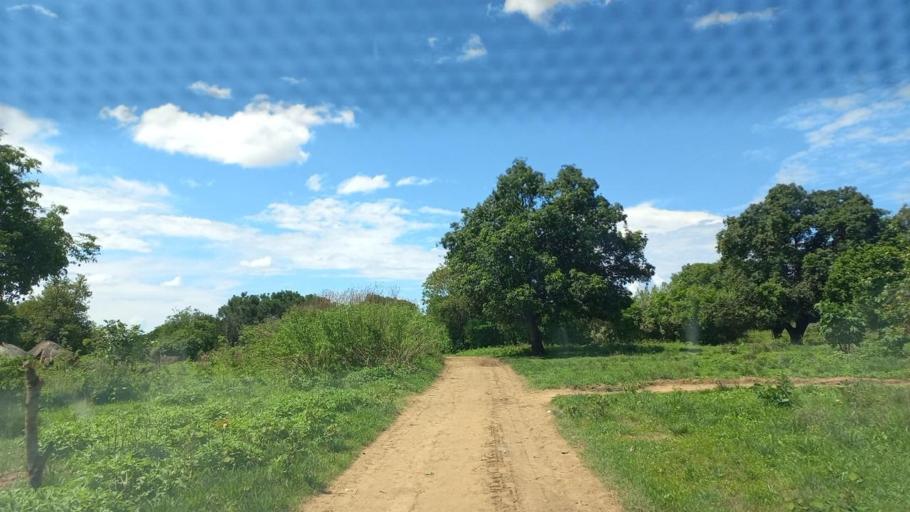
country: ZM
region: North-Western
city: Kabompo
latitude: -13.6180
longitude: 24.2098
